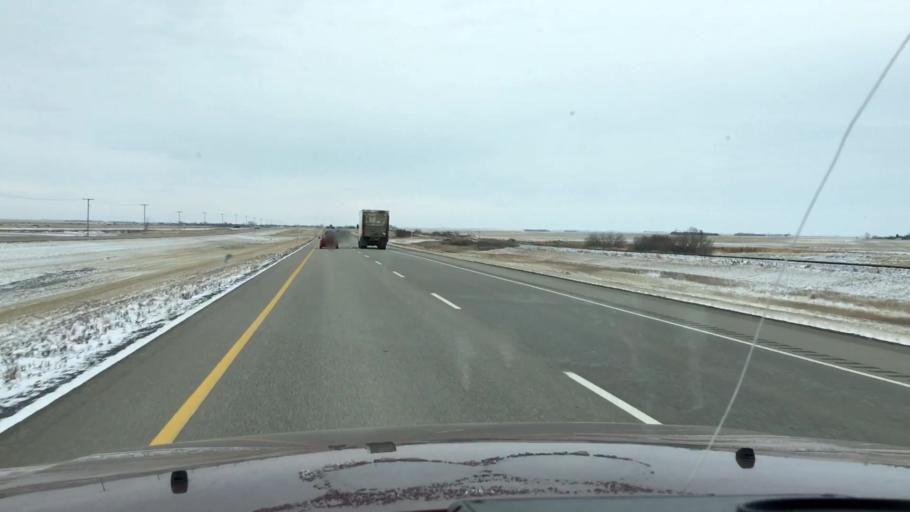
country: CA
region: Saskatchewan
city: Watrous
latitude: 51.1853
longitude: -105.9436
